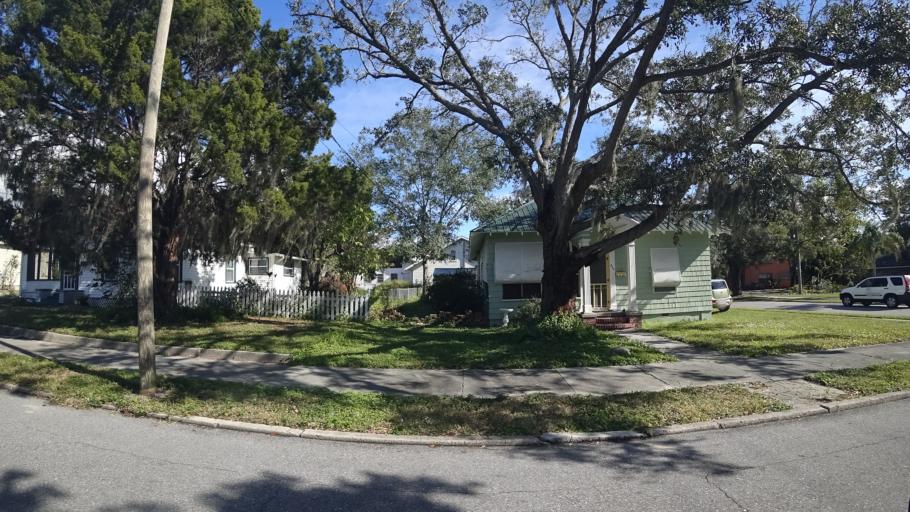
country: US
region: Florida
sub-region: Manatee County
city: Bradenton
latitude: 27.4939
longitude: -82.5805
